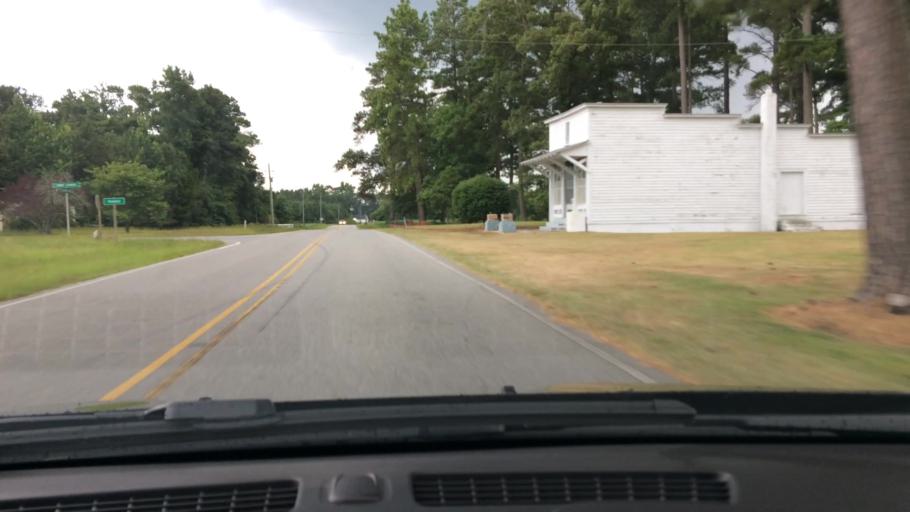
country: US
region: North Carolina
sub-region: Pitt County
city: Ayden
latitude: 35.4820
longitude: -77.3770
